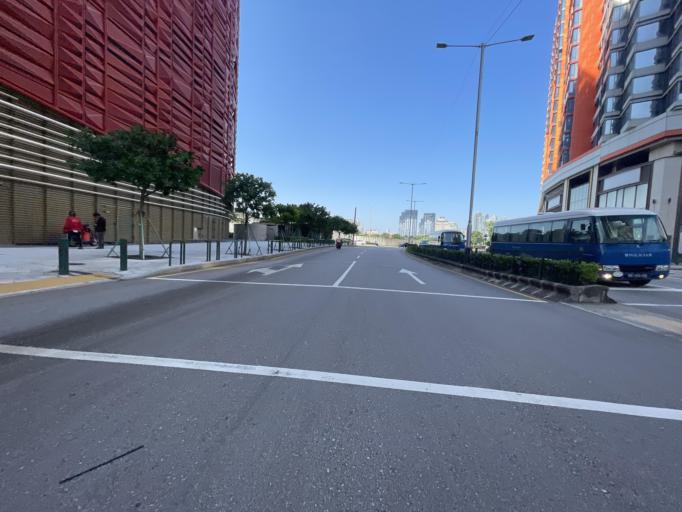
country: MO
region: Macau
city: Macau
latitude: 22.1293
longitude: 113.5582
